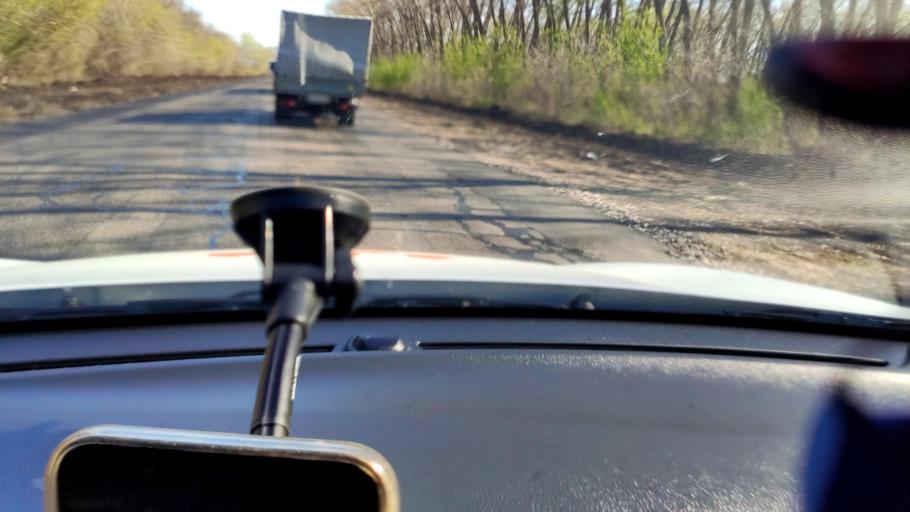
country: RU
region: Voronezj
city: Uryv-Pokrovka
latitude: 51.1946
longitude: 39.0851
